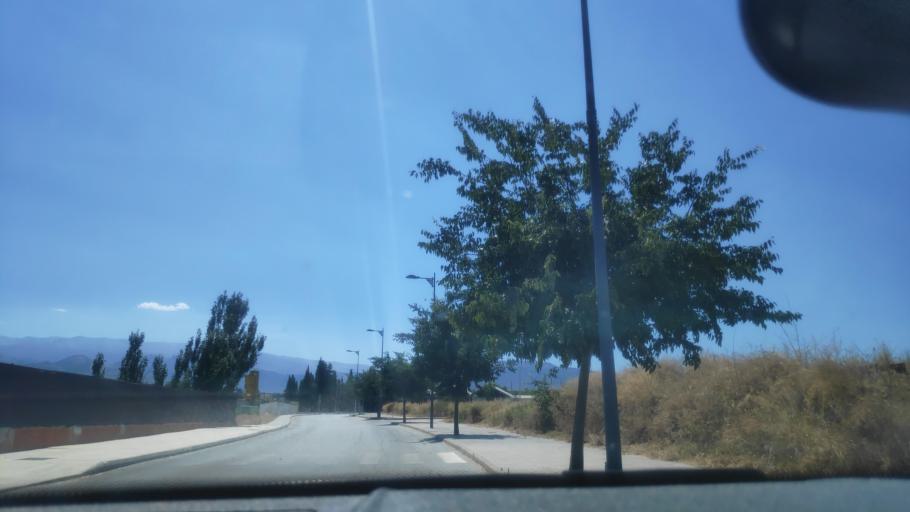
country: ES
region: Andalusia
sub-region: Provincia de Granada
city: Alhendin
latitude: 37.1033
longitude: -3.6526
